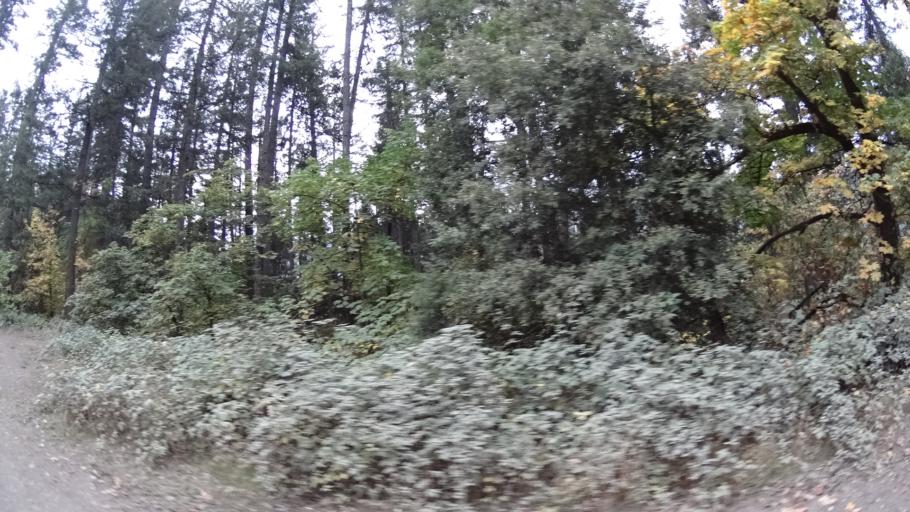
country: US
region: California
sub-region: Siskiyou County
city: Happy Camp
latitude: 41.7896
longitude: -123.3367
